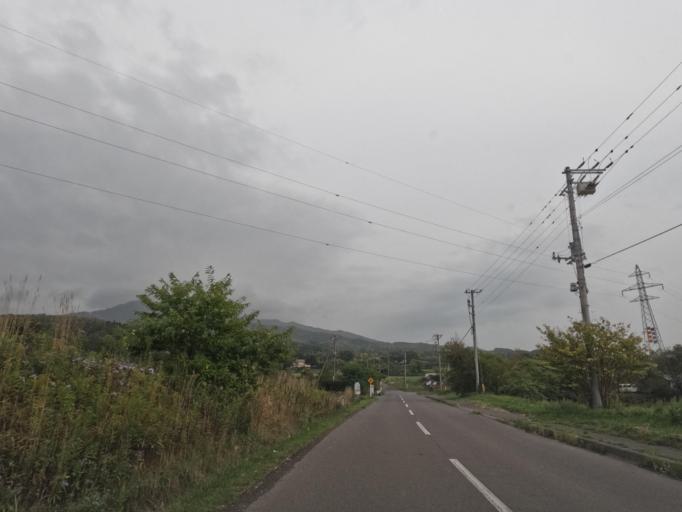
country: JP
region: Hokkaido
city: Date
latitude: 42.4550
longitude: 140.9055
